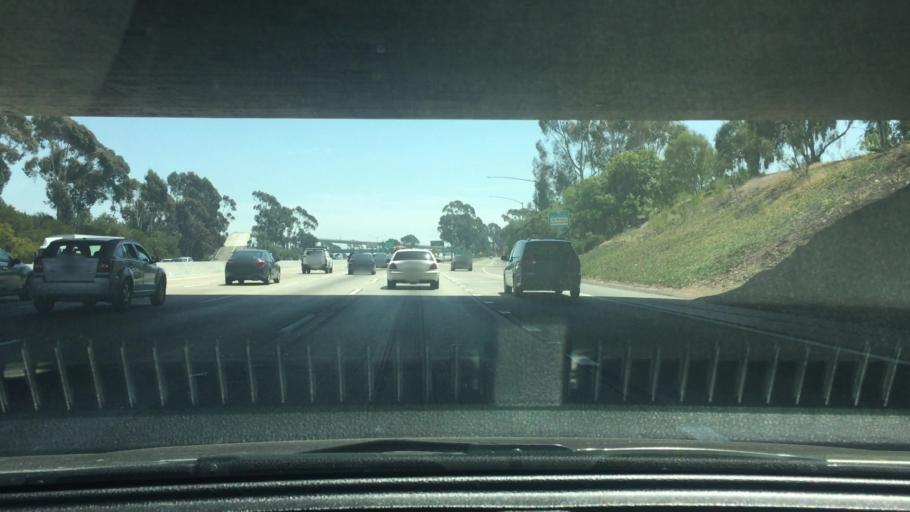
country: US
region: California
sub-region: San Diego County
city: National City
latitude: 32.6969
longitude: -117.0951
